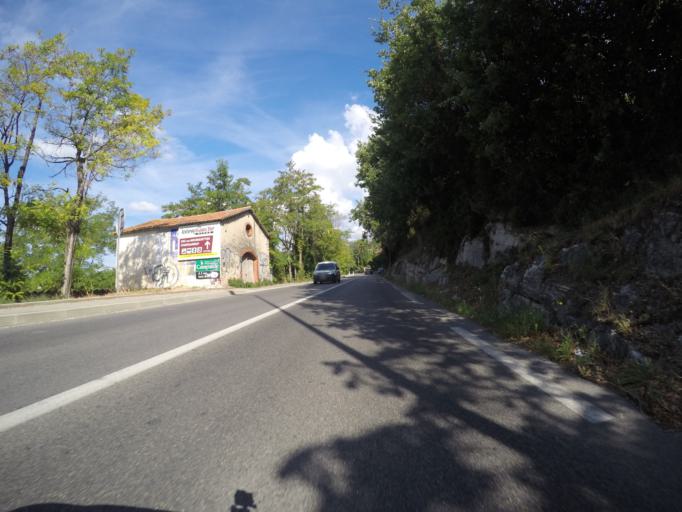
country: FR
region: Provence-Alpes-Cote d'Azur
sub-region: Departement des Alpes-Maritimes
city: Opio
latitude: 43.6741
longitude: 6.9889
